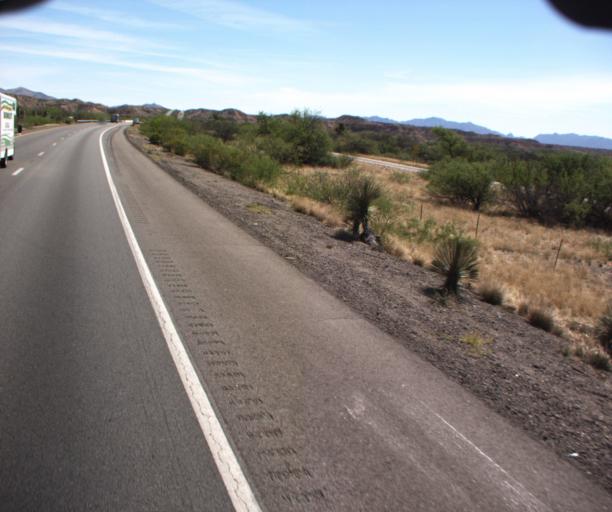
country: US
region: Arizona
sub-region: Cochise County
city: Benson
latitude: 31.9770
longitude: -110.2294
